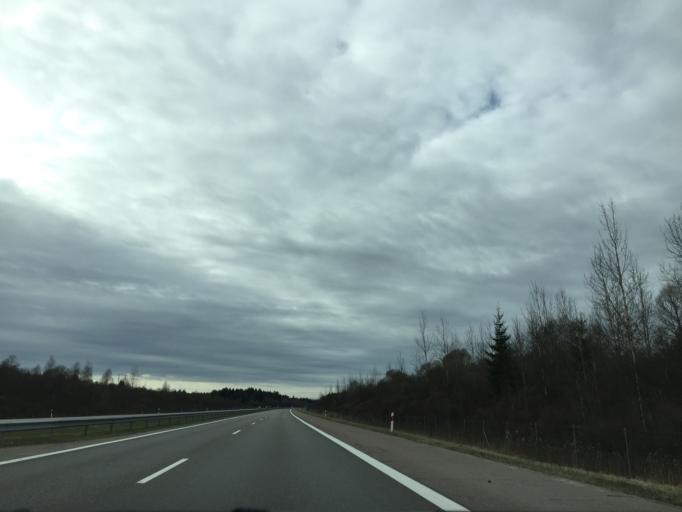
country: LT
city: Rietavas
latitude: 55.6110
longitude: 22.0440
